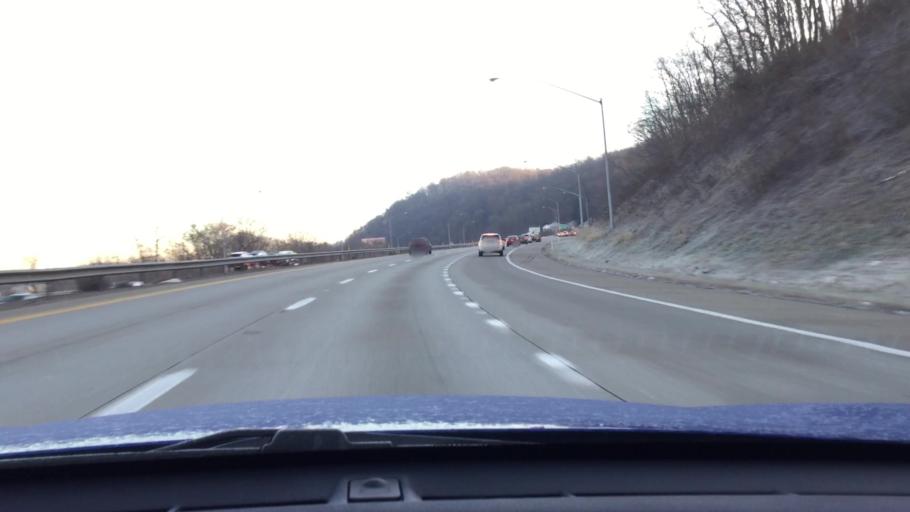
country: US
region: Pennsylvania
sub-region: Washington County
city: Canonsburg
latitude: 40.2564
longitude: -80.1799
